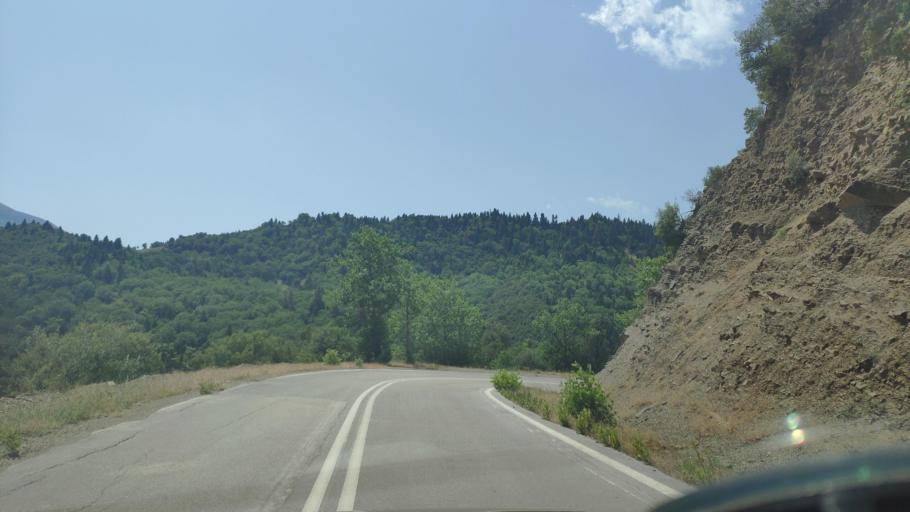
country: GR
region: Thessaly
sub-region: Nomos Kardhitsas
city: Anthiro
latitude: 39.2687
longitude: 21.3540
